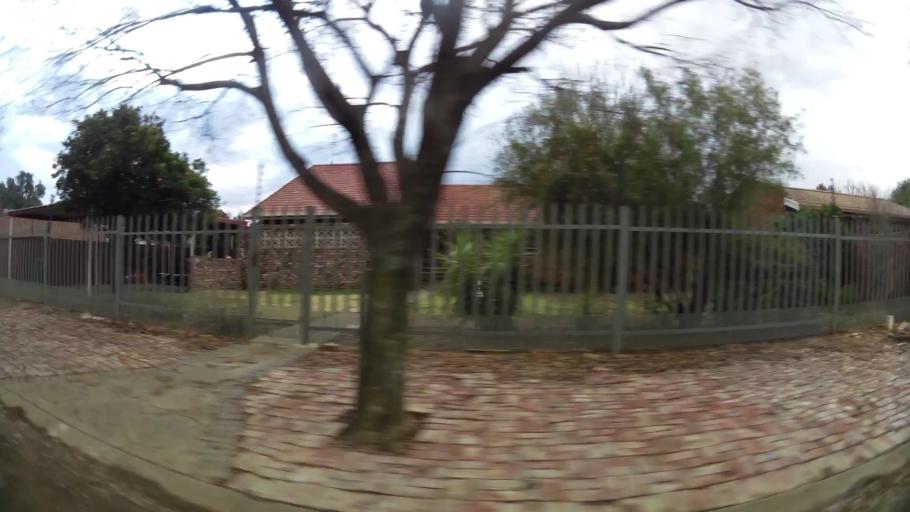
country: ZA
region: Orange Free State
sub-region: Lejweleputswa District Municipality
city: Welkom
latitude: -27.9513
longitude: 26.7273
